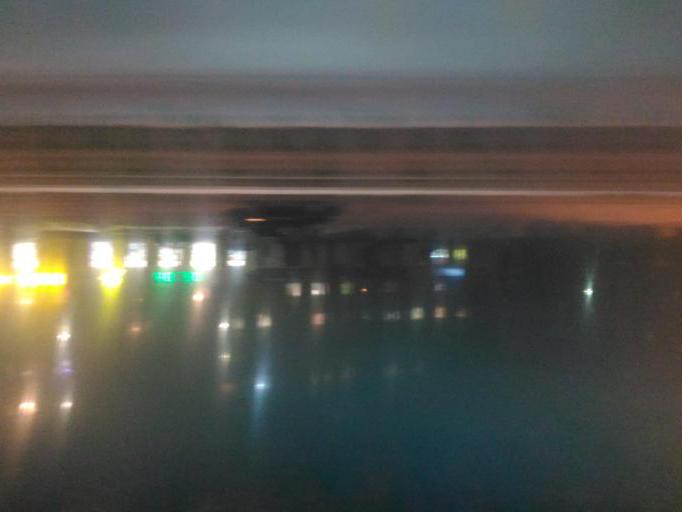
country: RU
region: Ulyanovsk
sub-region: Ulyanovskiy Rayon
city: Ulyanovsk
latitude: 54.3492
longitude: 48.3673
